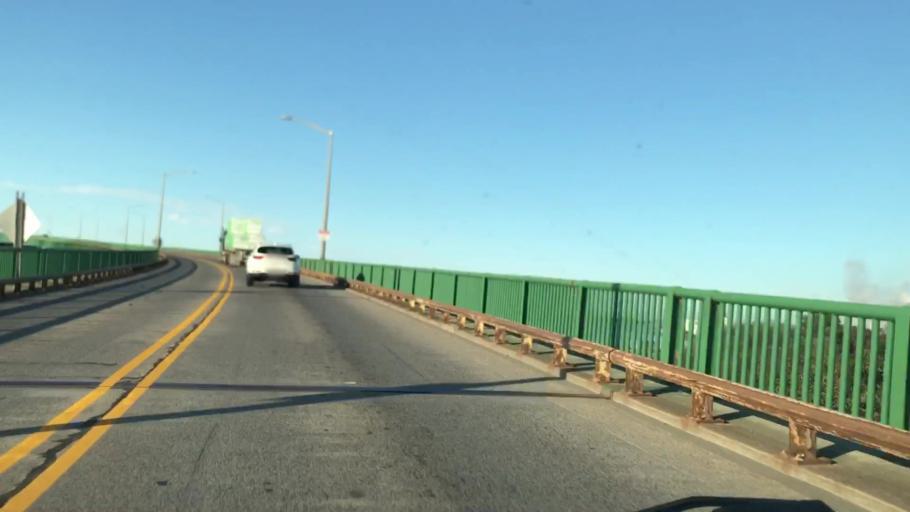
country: CA
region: Ontario
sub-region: Algoma
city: Sault Ste. Marie
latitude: 46.5177
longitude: -84.3555
